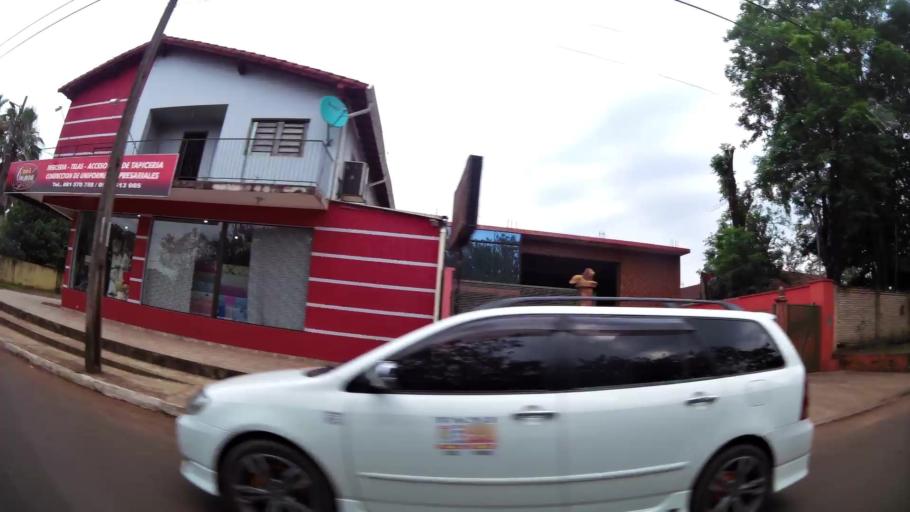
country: PY
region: Alto Parana
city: Presidente Franco
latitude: -25.5204
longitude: -54.6444
